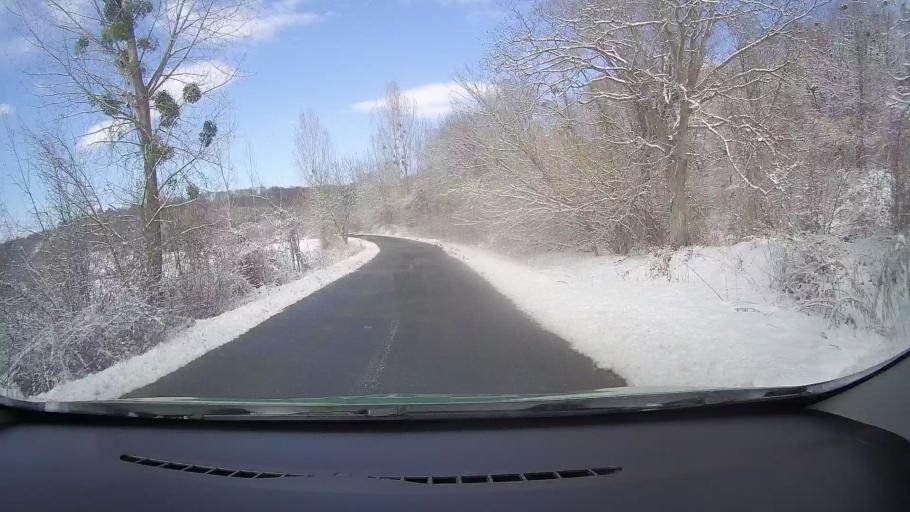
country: RO
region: Sibiu
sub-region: Comuna Mosna
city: Mosna
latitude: 46.0113
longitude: 24.4221
